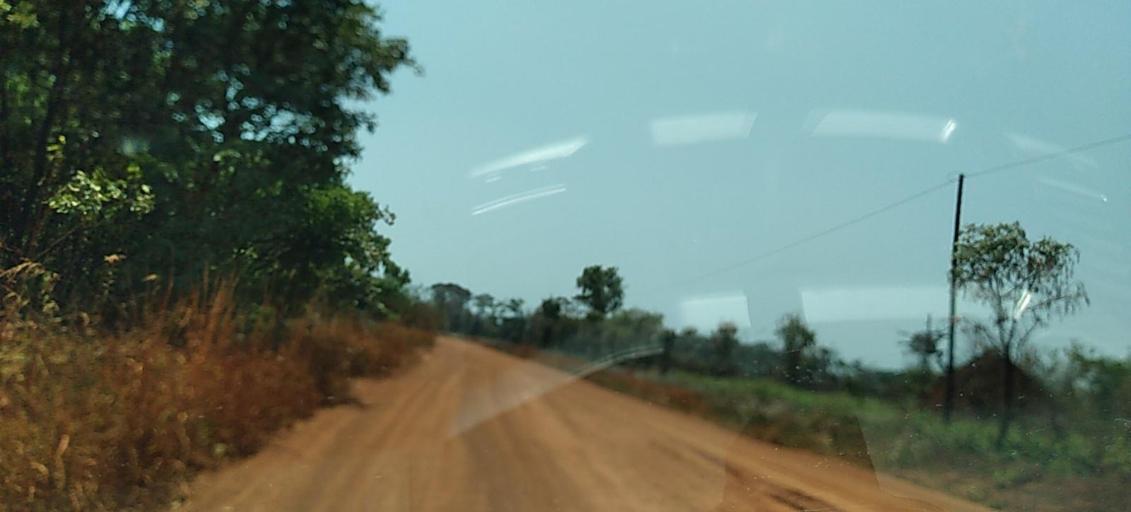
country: CD
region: Katanga
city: Kipushi
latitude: -11.9862
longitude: 26.8764
